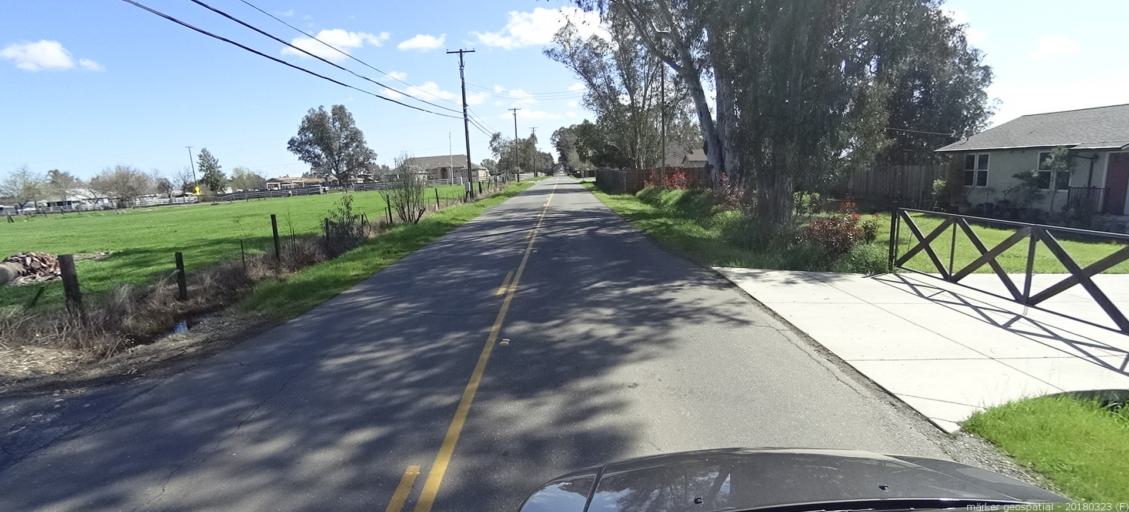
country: US
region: California
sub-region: Sacramento County
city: Rio Linda
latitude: 38.6762
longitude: -121.4165
